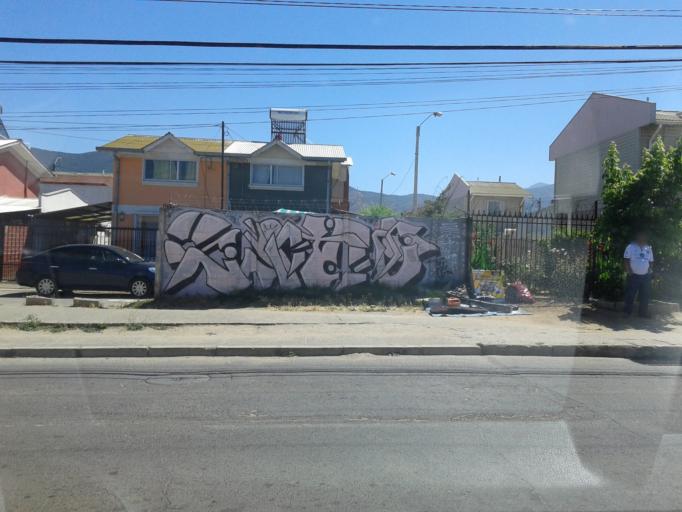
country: CL
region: Valparaiso
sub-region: Provincia de Marga Marga
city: Limache
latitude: -33.0091
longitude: -71.2553
